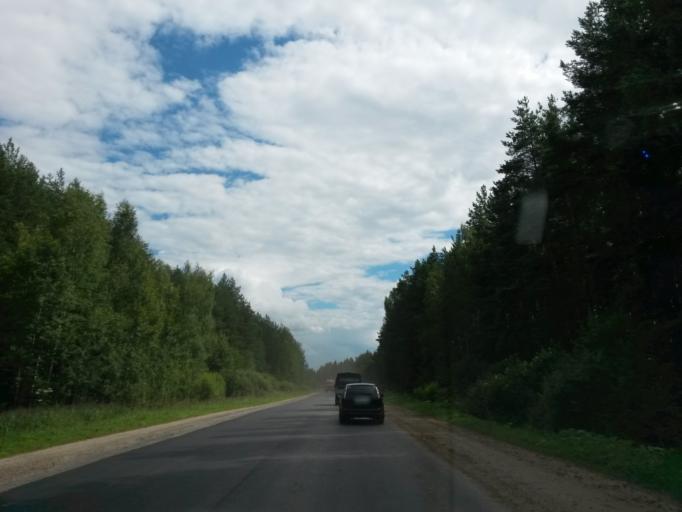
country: RU
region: Ivanovo
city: Novo-Talitsy
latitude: 57.0184
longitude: 40.7800
